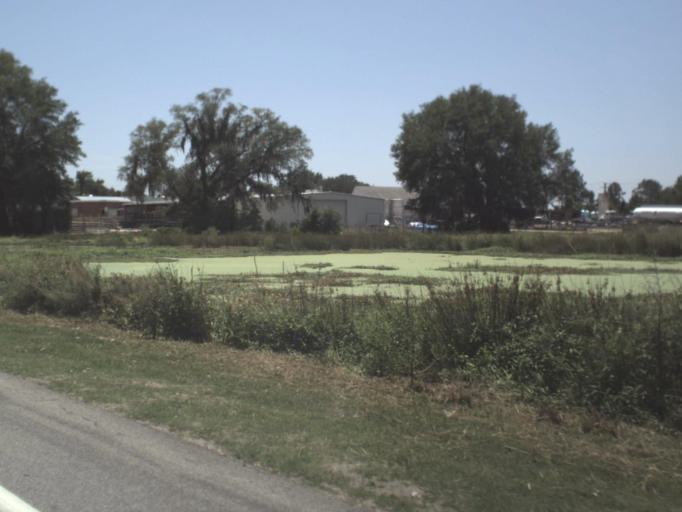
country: US
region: Florida
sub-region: Suwannee County
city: Live Oak
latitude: 30.3074
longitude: -83.0095
